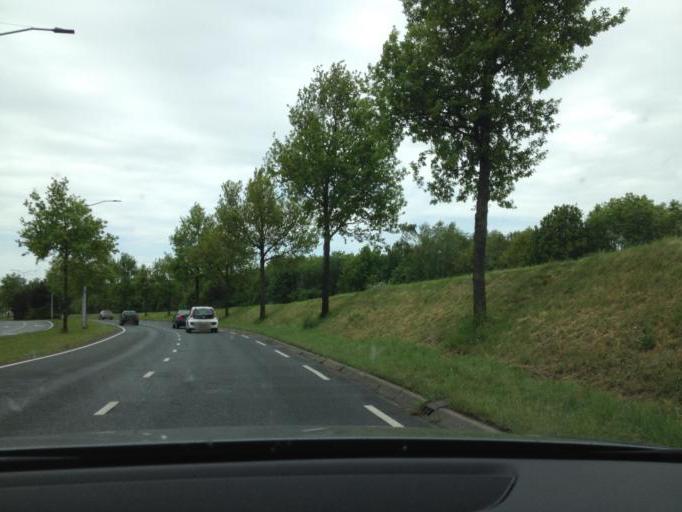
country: NL
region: Flevoland
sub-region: Gemeente Almere
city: Almere Stad
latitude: 52.3665
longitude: 5.2473
